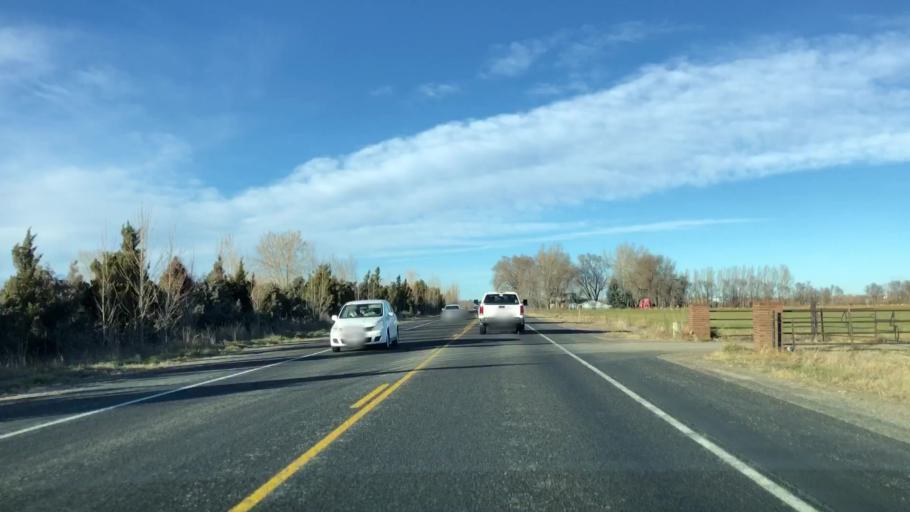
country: US
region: Colorado
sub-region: Weld County
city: Windsor
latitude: 40.5054
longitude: -104.9818
